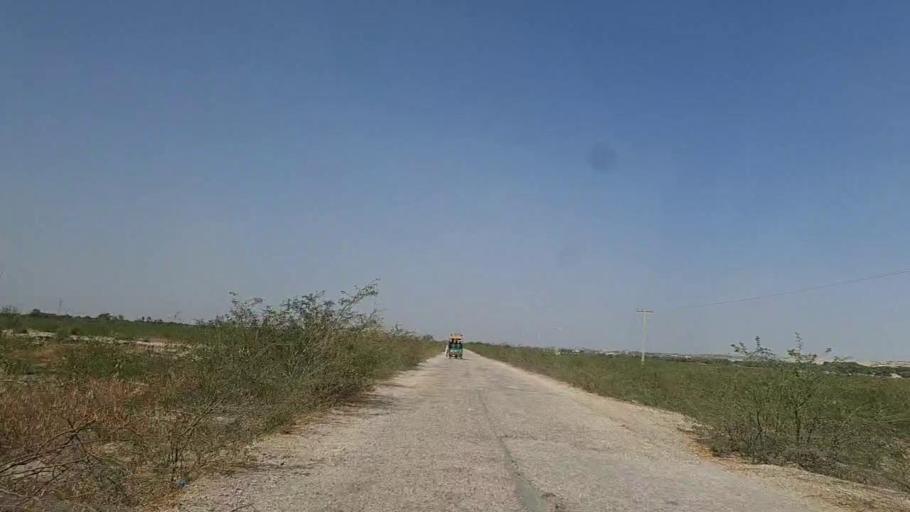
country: PK
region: Sindh
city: Naukot
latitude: 24.6422
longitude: 69.2879
